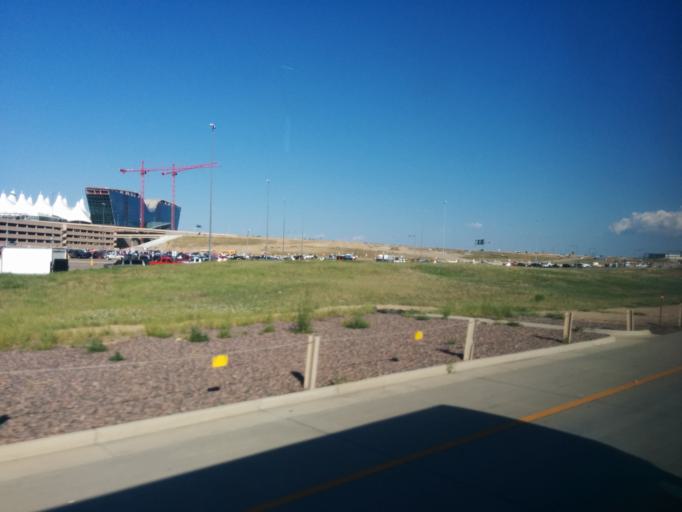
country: US
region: Colorado
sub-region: Weld County
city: Lochbuie
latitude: 39.8455
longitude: -104.6809
